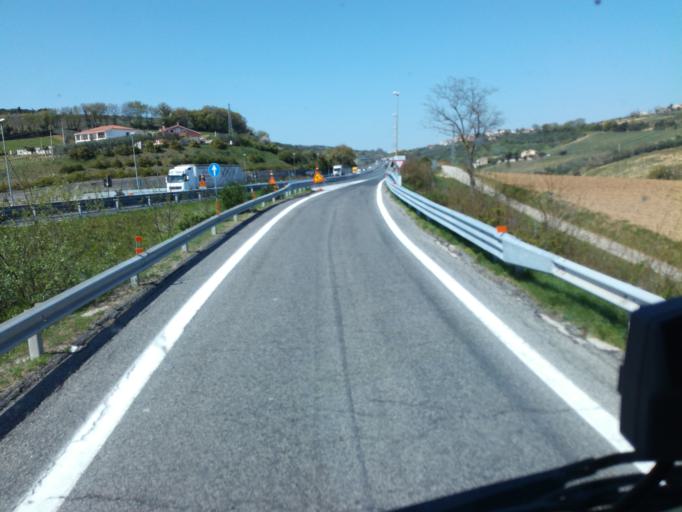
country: IT
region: Abruzzo
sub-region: Provincia di Chieti
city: Francavilla al Mare
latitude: 42.3988
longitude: 14.2877
